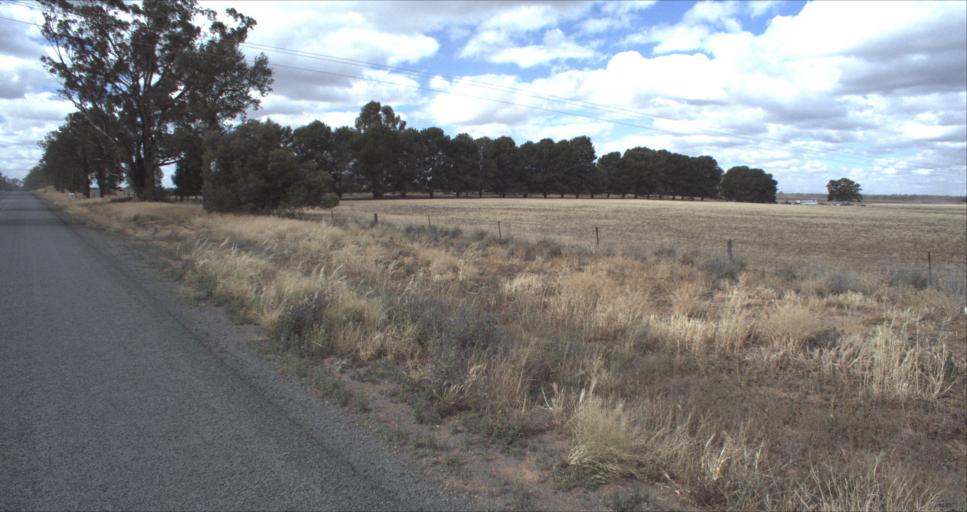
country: AU
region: New South Wales
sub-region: Leeton
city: Leeton
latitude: -34.6618
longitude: 146.3492
